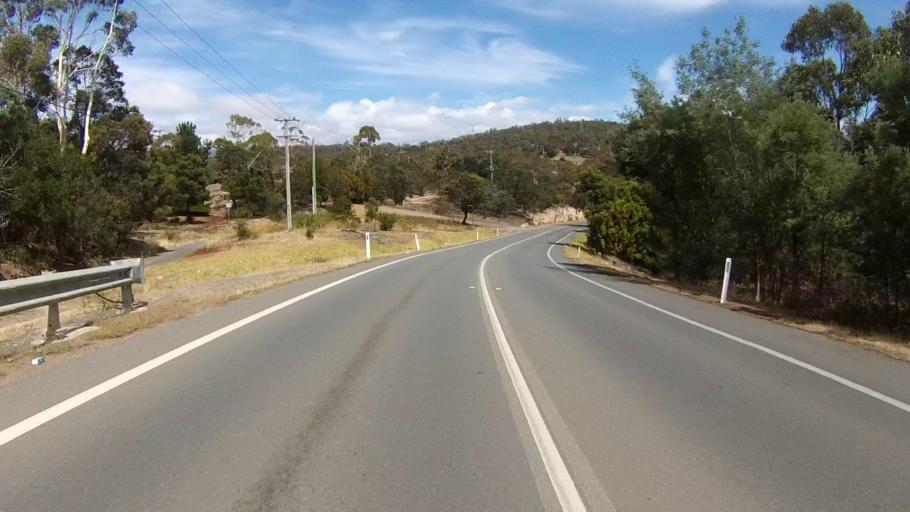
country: AU
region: Tasmania
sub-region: Clarence
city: Lindisfarne
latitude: -42.8237
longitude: 147.3484
